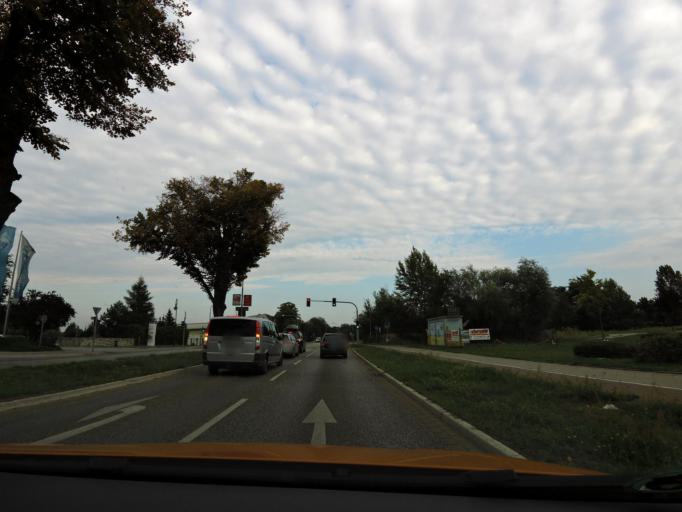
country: DE
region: Brandenburg
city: Werder
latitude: 52.3643
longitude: 12.9403
